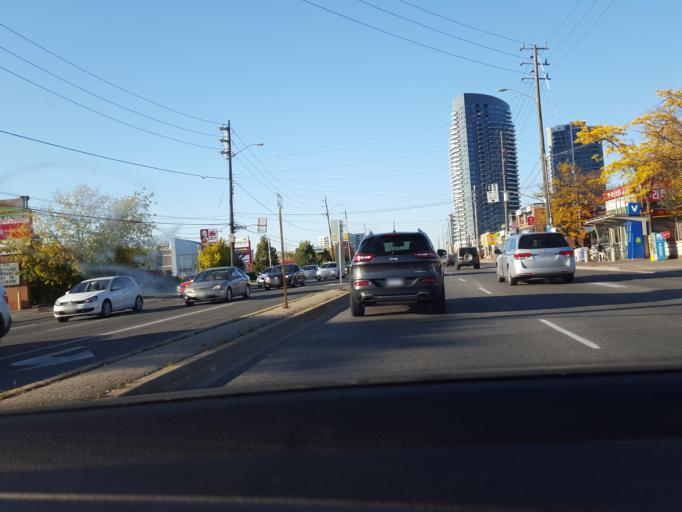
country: CA
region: Ontario
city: North York
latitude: 43.7982
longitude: -79.4200
